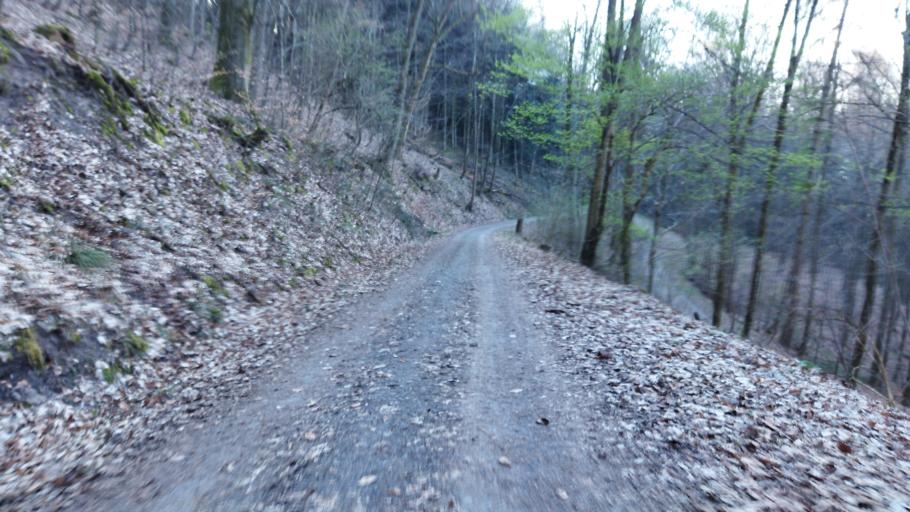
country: DE
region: Baden-Wuerttemberg
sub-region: Karlsruhe Region
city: Sternenfels
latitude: 49.0474
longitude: 8.8618
